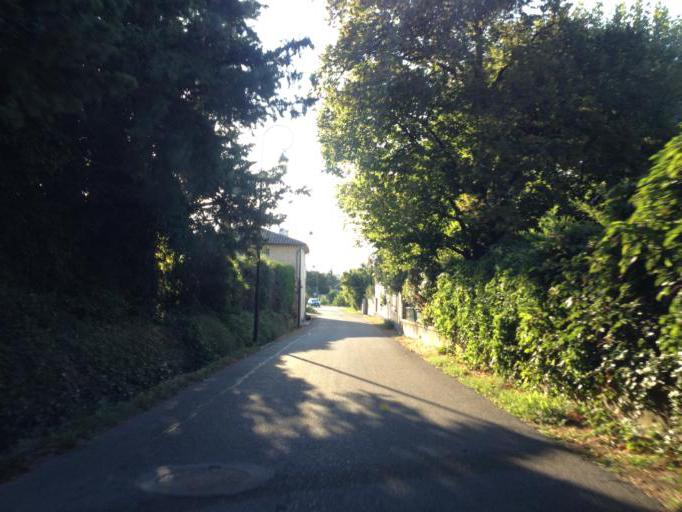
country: FR
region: Provence-Alpes-Cote d'Azur
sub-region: Departement du Vaucluse
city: Sablet
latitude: 44.1930
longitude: 5.0024
